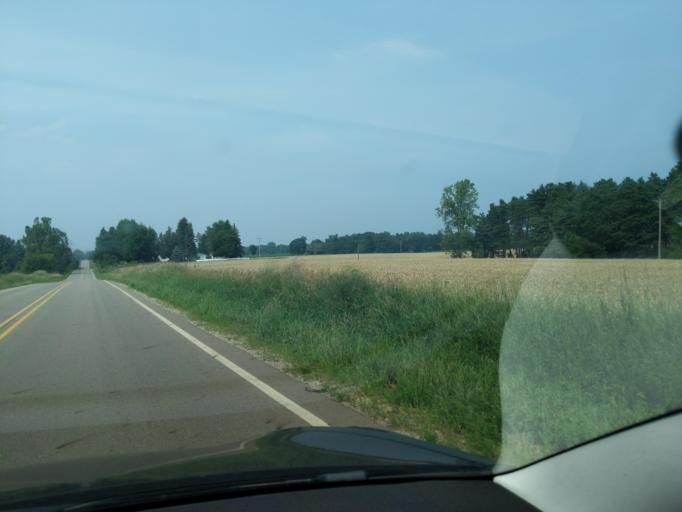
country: US
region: Michigan
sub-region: Clinton County
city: DeWitt
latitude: 42.8792
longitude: -84.5722
